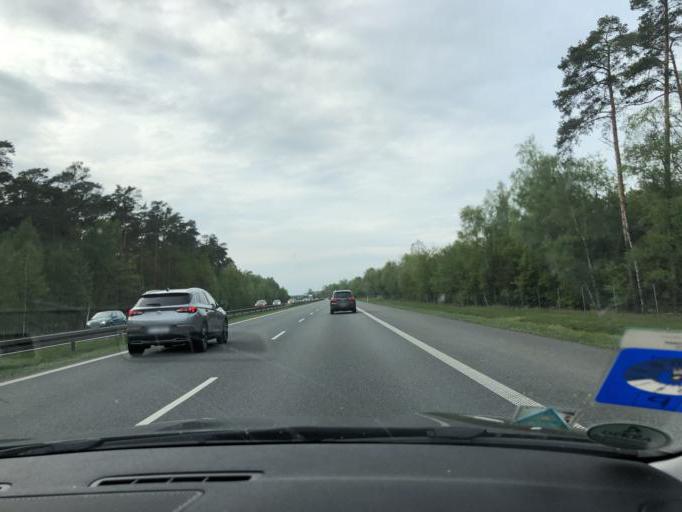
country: PL
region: Opole Voivodeship
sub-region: Powiat brzeski
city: Lewin Brzeski
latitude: 50.6996
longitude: 17.6204
